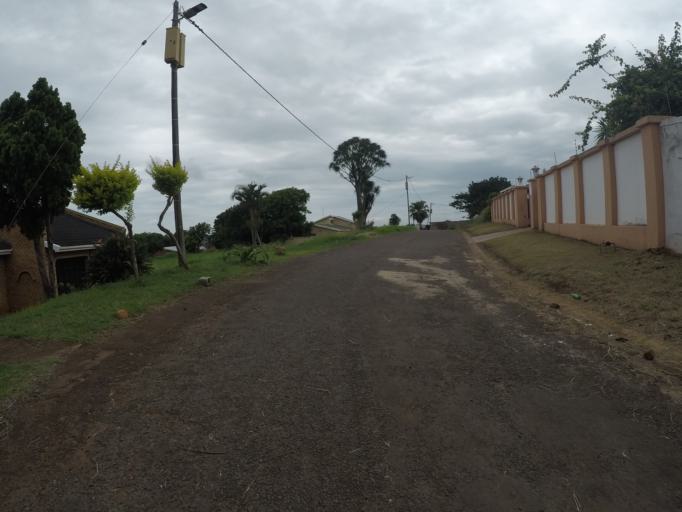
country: ZA
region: KwaZulu-Natal
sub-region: uThungulu District Municipality
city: Empangeni
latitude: -28.7697
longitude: 31.8632
